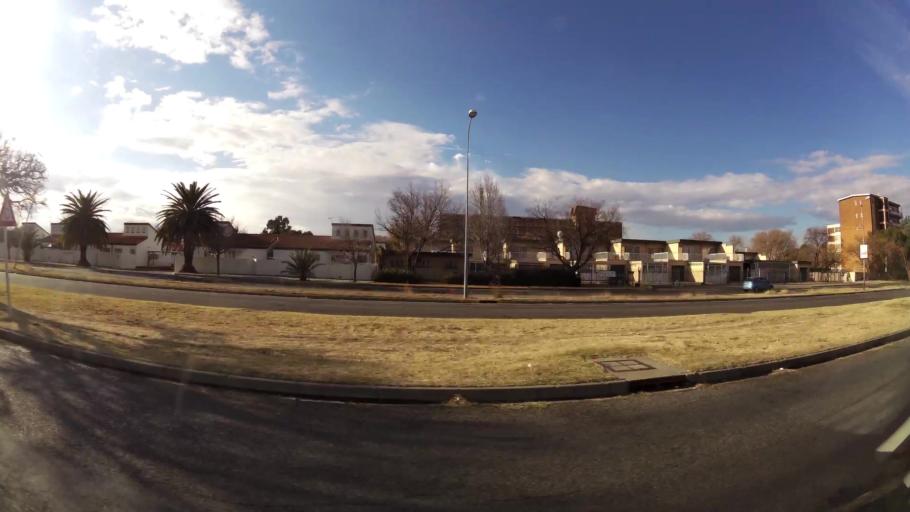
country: ZA
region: Orange Free State
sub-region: Lejweleputswa District Municipality
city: Welkom
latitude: -27.9836
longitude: 26.7296
